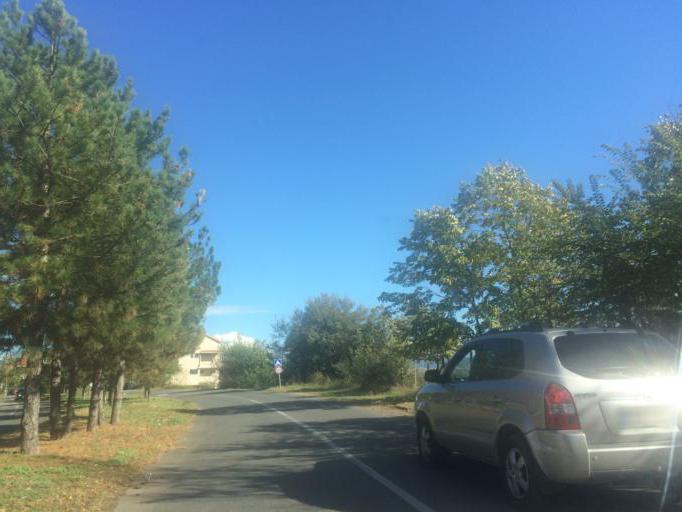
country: MK
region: Kocani
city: Orizari
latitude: 41.9133
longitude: 22.4364
